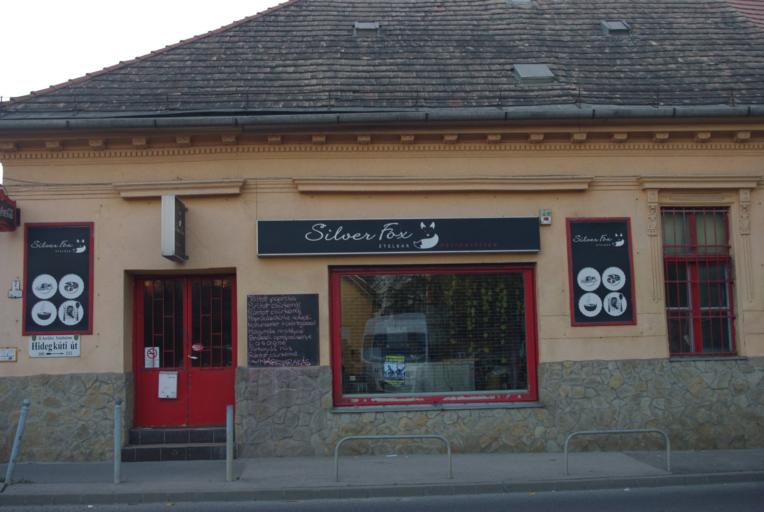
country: HU
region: Pest
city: Solymar
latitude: 47.5640
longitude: 18.9620
